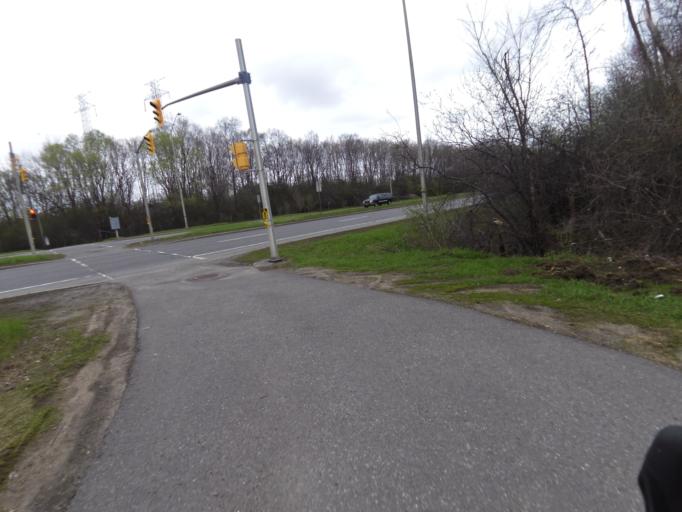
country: CA
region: Ontario
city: Bells Corners
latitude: 45.3300
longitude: -75.7449
